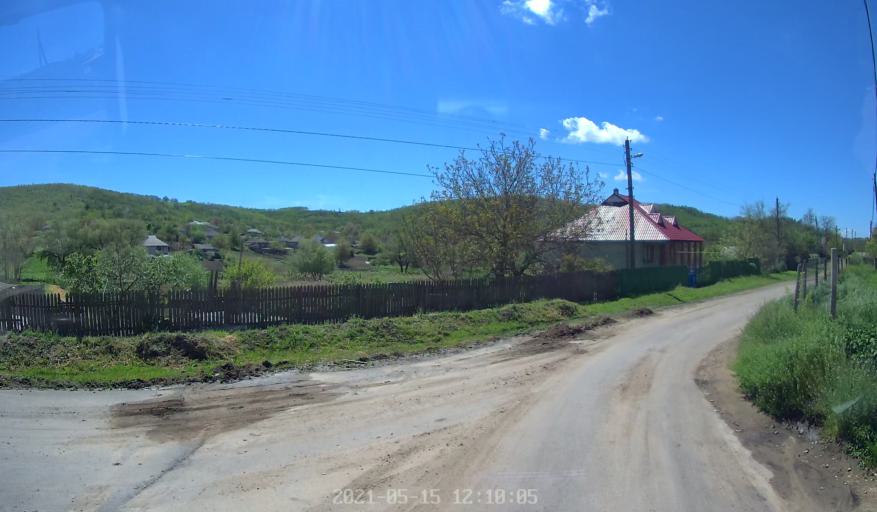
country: MD
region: Hincesti
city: Hincesti
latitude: 46.7970
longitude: 28.5411
